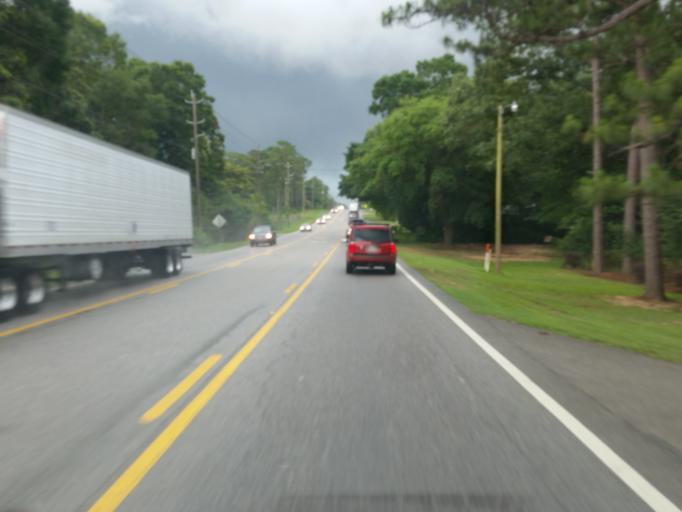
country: US
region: Alabama
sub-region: Mobile County
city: Chickasaw
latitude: 30.7910
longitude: -88.3001
